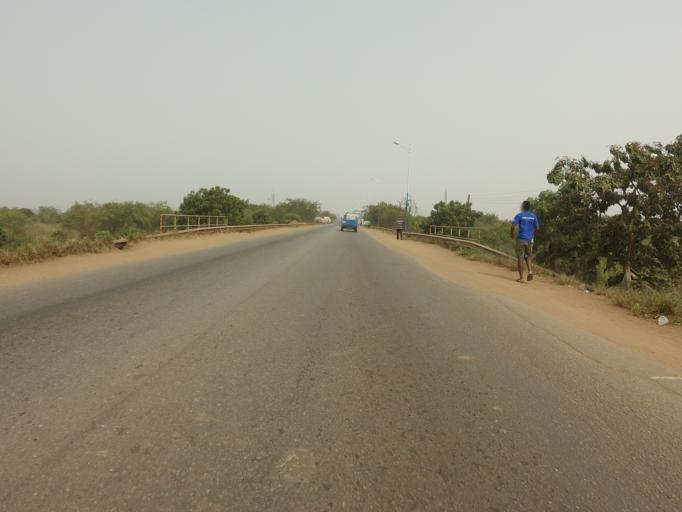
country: GH
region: Greater Accra
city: Tema
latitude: 5.7654
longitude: 0.0586
